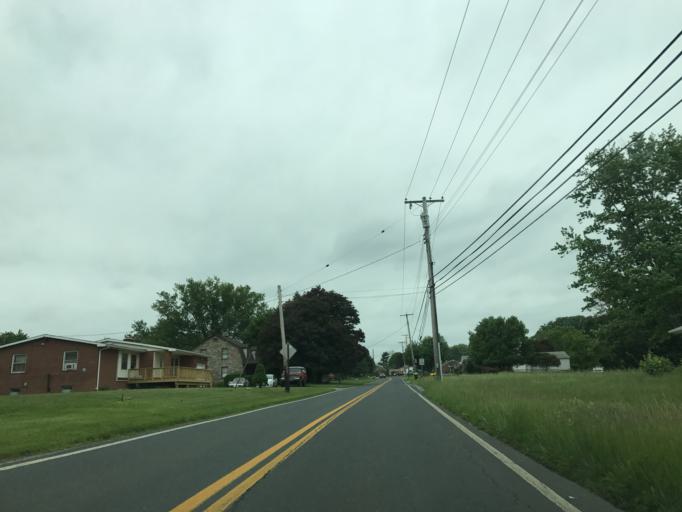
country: US
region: Maryland
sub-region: Carroll County
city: Hampstead
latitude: 39.6186
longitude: -76.8484
